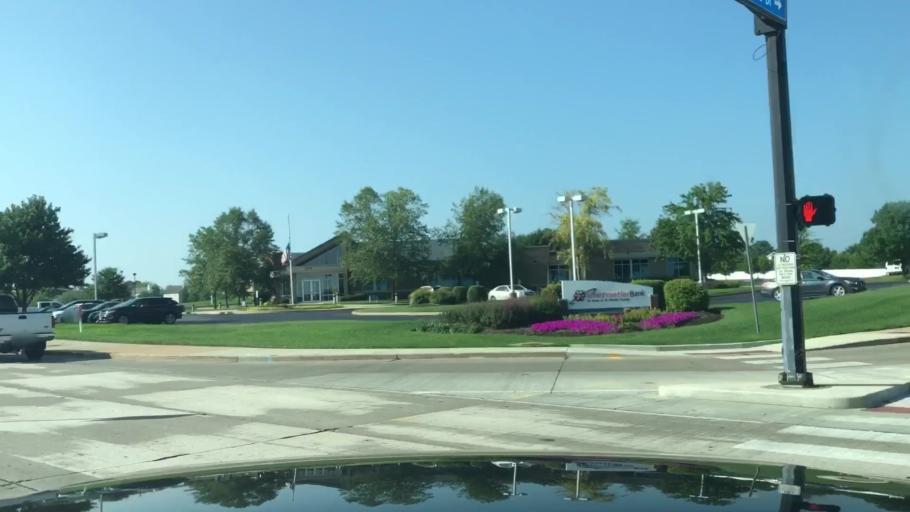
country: US
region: Missouri
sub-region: Saint Charles County
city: Saint Charles
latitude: 38.7756
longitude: -90.5275
